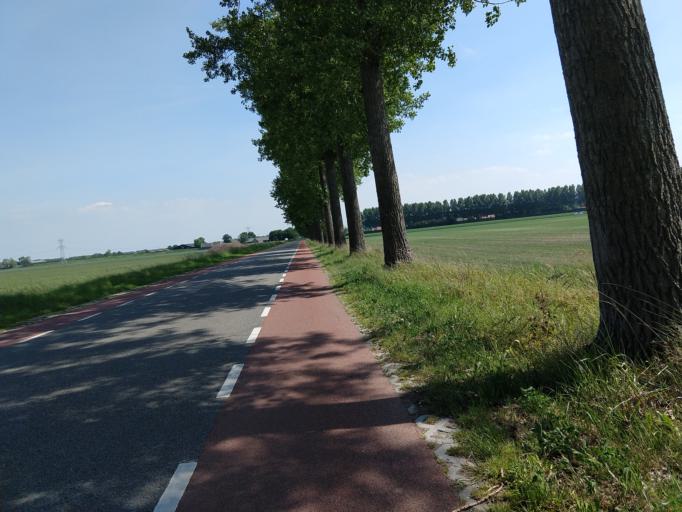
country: NL
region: Zeeland
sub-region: Gemeente Borsele
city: Borssele
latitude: 51.4392
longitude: 3.8009
